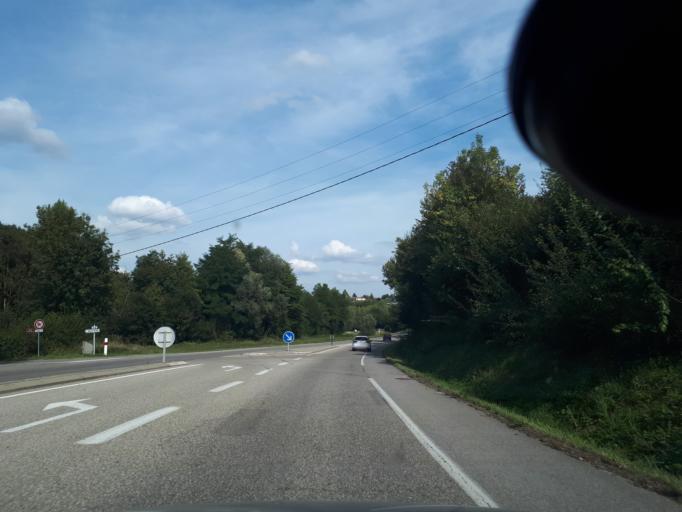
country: FR
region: Rhone-Alpes
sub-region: Departement de l'Isere
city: Maubec
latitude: 45.5523
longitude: 5.2681
